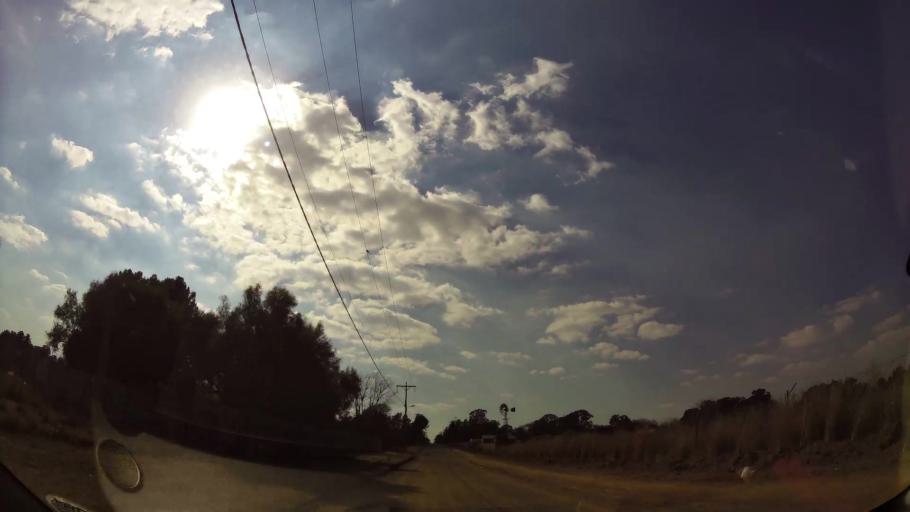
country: ZA
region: Gauteng
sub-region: Ekurhuleni Metropolitan Municipality
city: Benoni
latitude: -26.0941
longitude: 28.3538
